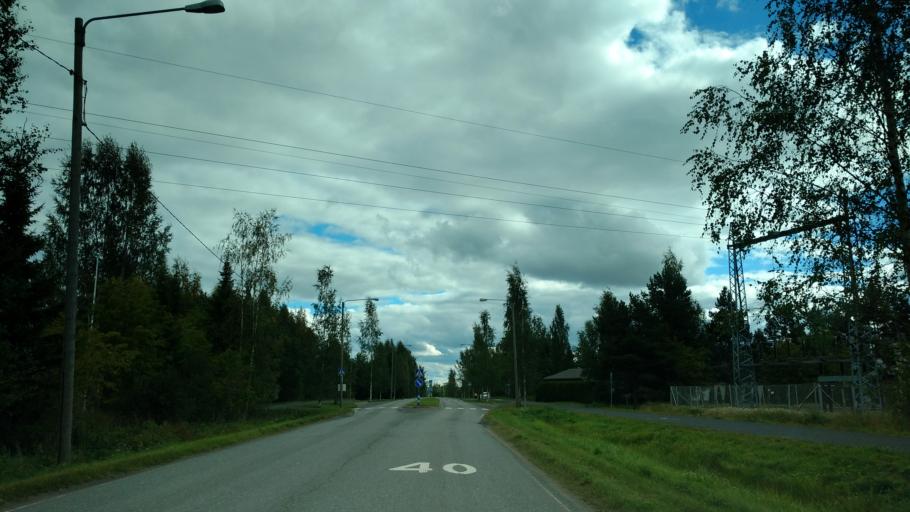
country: FI
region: Haeme
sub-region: Forssa
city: Ypaejae
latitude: 60.8074
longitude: 23.2739
